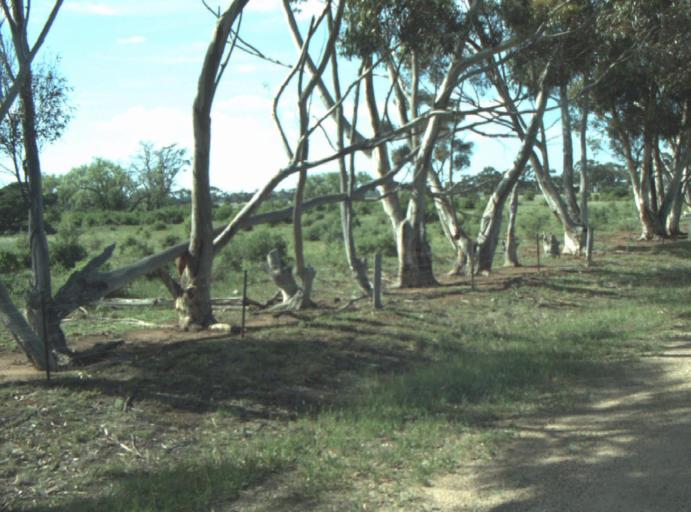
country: AU
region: Victoria
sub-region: Greater Geelong
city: Lara
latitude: -37.9827
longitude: 144.4223
